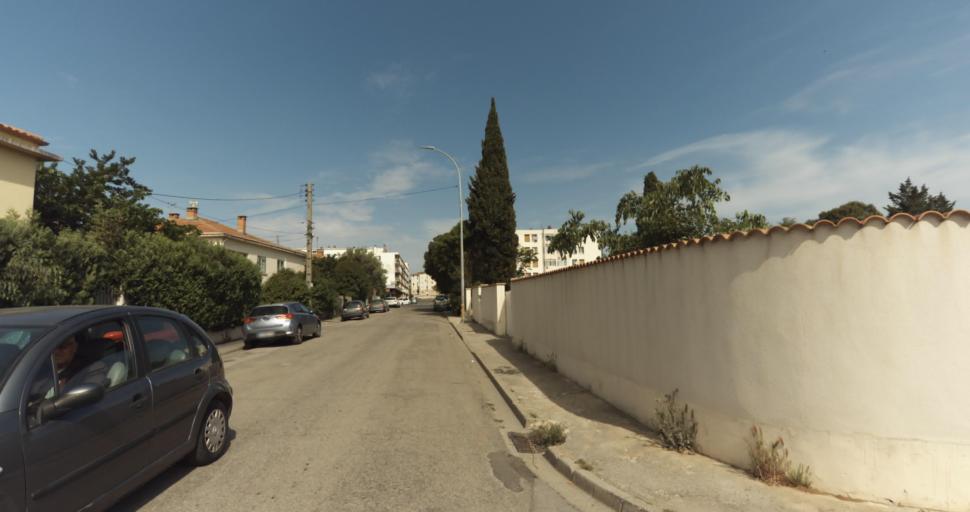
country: FR
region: Languedoc-Roussillon
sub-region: Departement du Gard
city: Rodilhan
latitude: 43.8545
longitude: 4.4002
